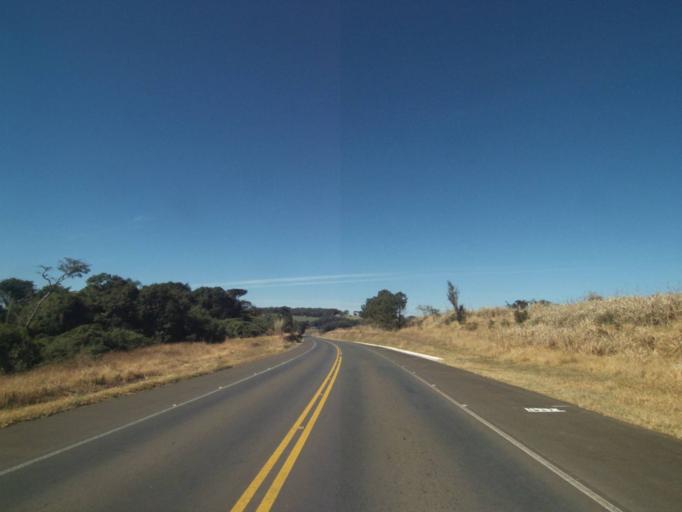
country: BR
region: Parana
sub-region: Tibagi
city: Tibagi
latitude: -24.7708
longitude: -50.4665
